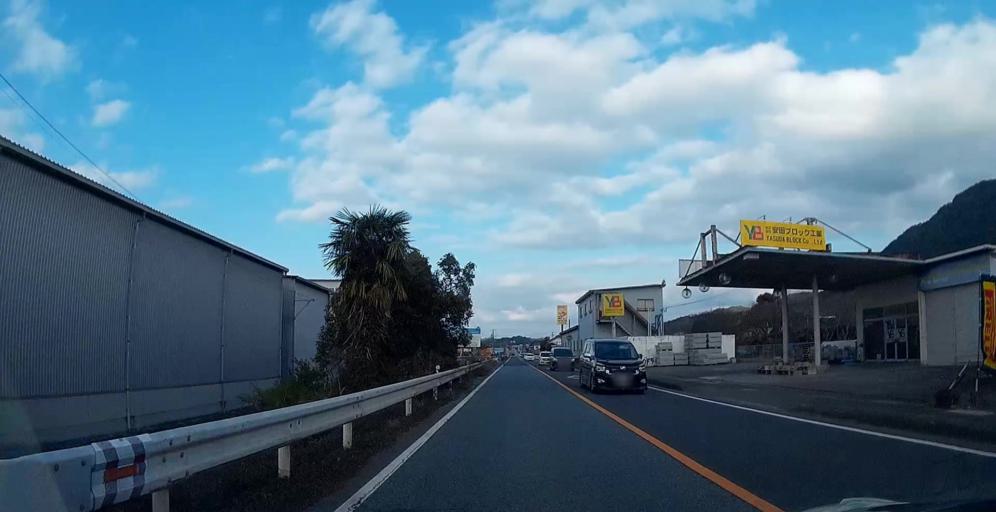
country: JP
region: Kumamoto
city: Yatsushiro
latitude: 32.5308
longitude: 130.6630
